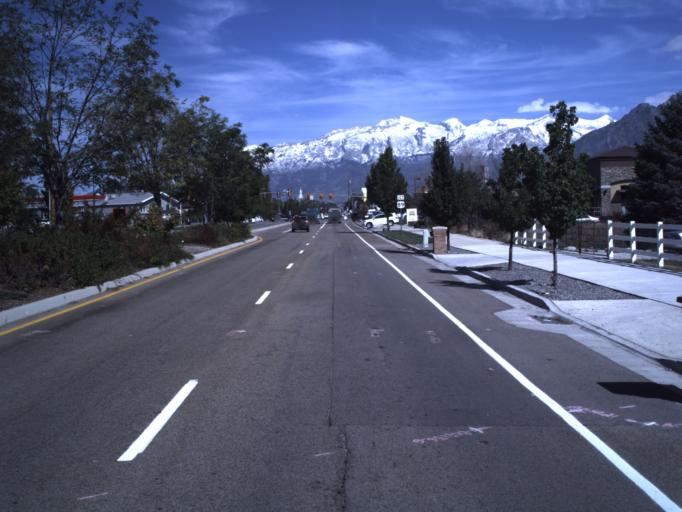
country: US
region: Utah
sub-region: Utah County
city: American Fork
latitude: 40.3682
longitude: -111.7691
